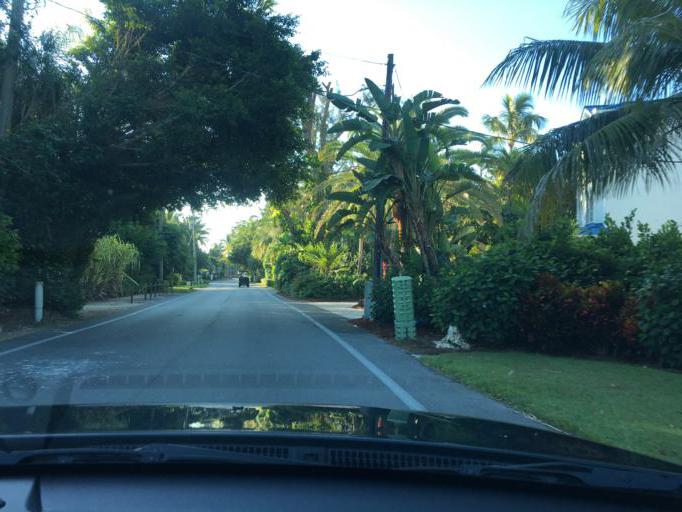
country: US
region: Florida
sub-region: Lee County
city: Pine Island Center
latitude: 26.5446
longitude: -82.1971
